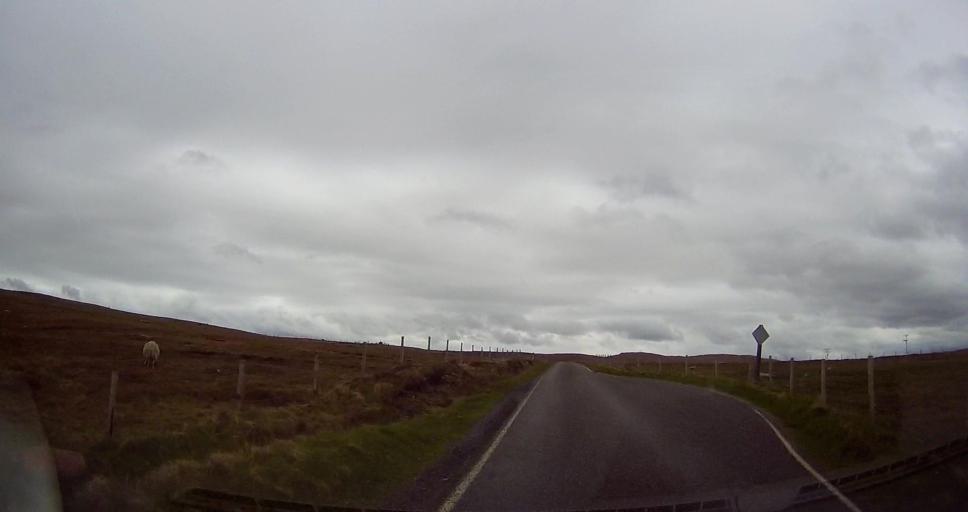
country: GB
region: Scotland
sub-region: Shetland Islands
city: Lerwick
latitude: 60.4862
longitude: -1.4848
